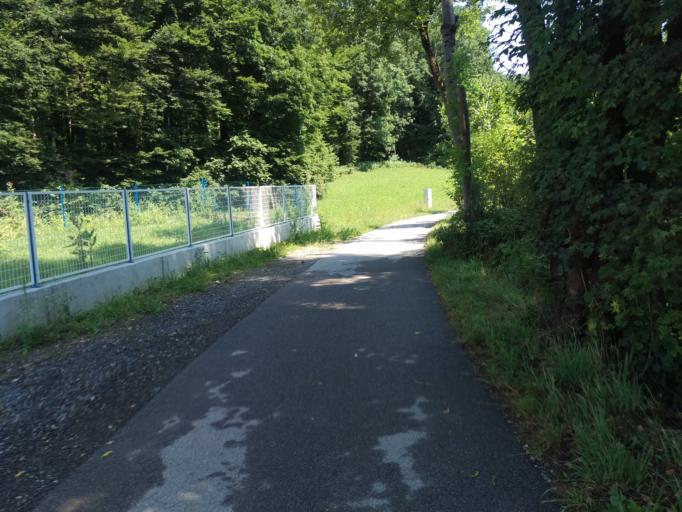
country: AT
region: Styria
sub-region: Politischer Bezirk Graz-Umgebung
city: Stattegg
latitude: 47.1266
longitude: 15.4436
